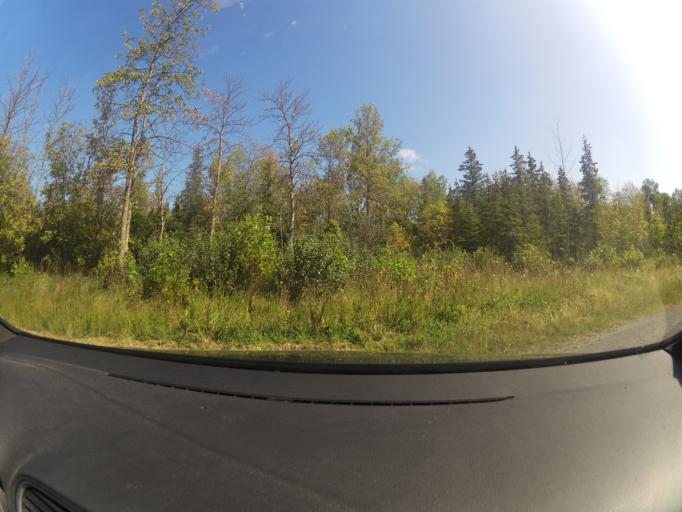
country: CA
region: Ontario
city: Arnprior
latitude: 45.3330
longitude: -76.2559
